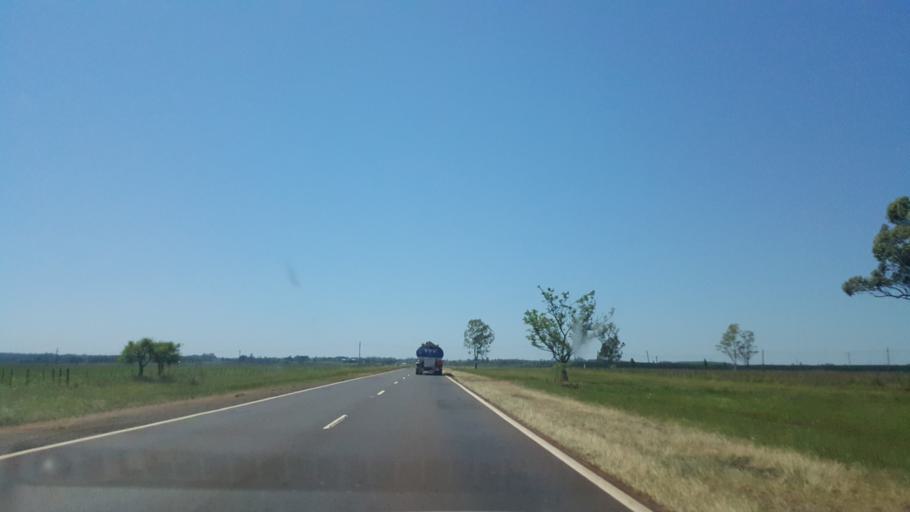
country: AR
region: Corrientes
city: Santo Tome
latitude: -28.5227
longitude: -56.1054
